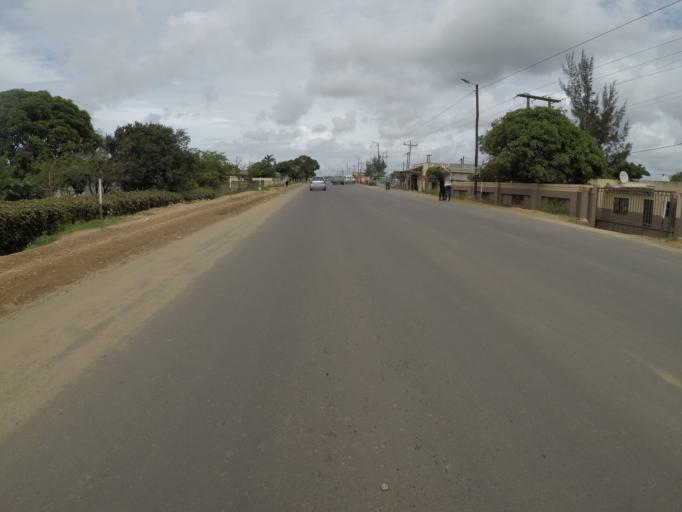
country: ZA
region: KwaZulu-Natal
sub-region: uThungulu District Municipality
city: eSikhawini
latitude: -28.8693
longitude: 31.9033
